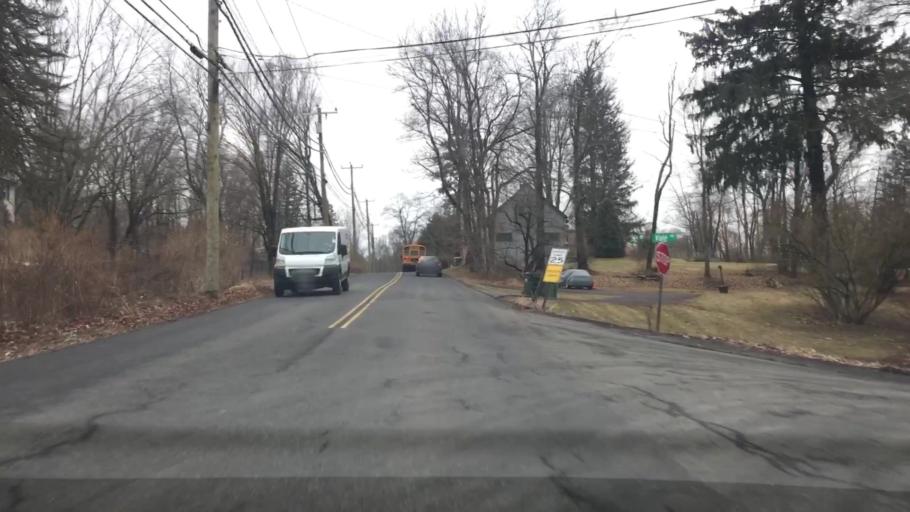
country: US
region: Connecticut
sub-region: Fairfield County
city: Bethel
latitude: 41.4426
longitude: -73.3929
